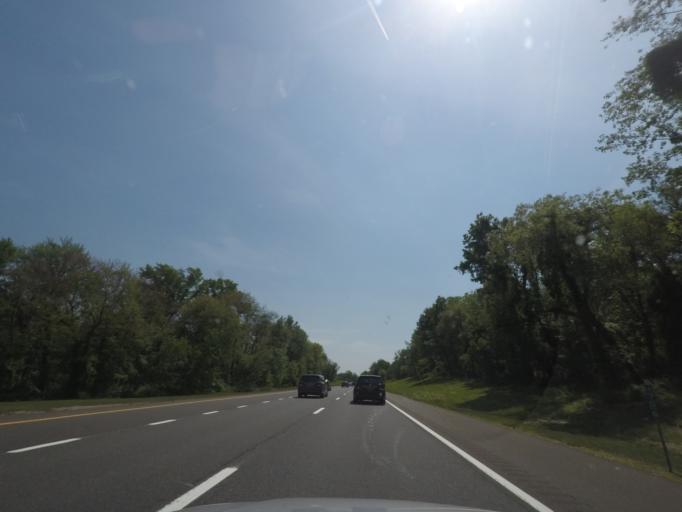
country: US
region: New Jersey
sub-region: Bergen County
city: Woodcliff Lake
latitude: 41.0440
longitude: -74.0694
